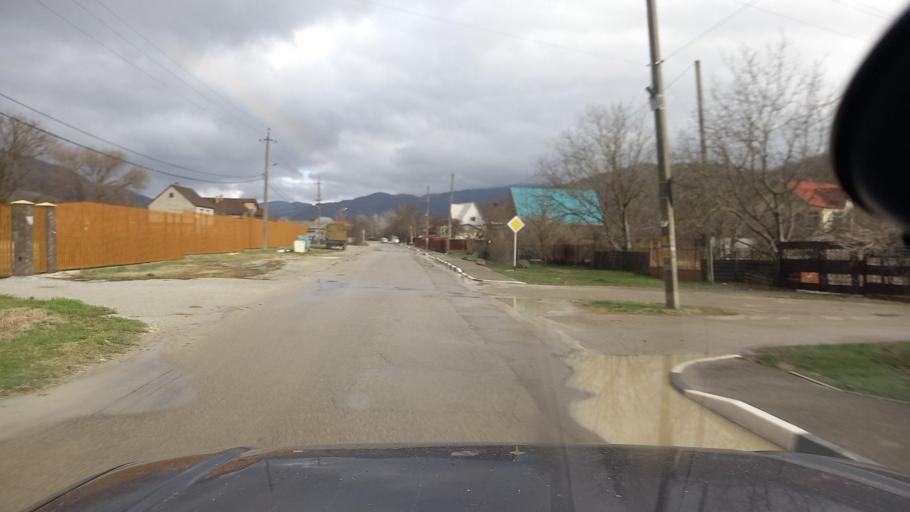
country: RU
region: Krasnodarskiy
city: Pshada
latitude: 44.4785
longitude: 38.4010
